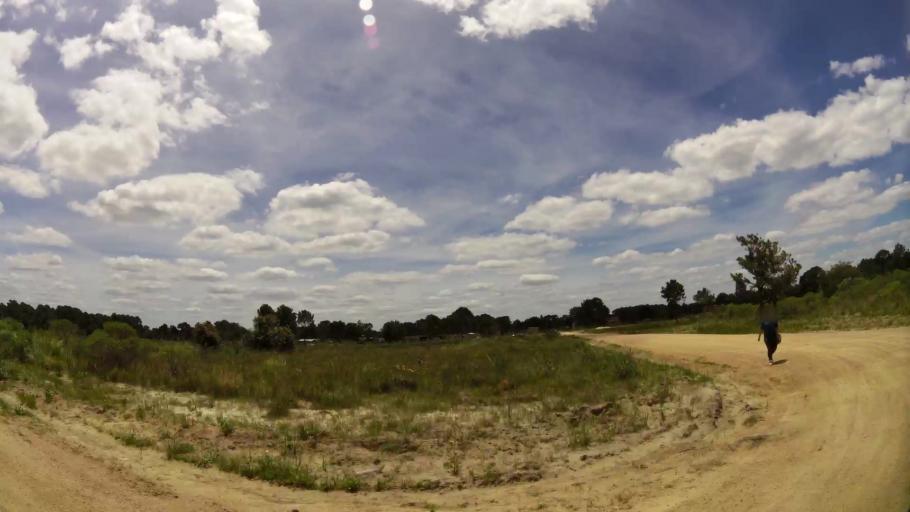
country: UY
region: Canelones
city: Pando
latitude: -34.8084
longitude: -55.9445
